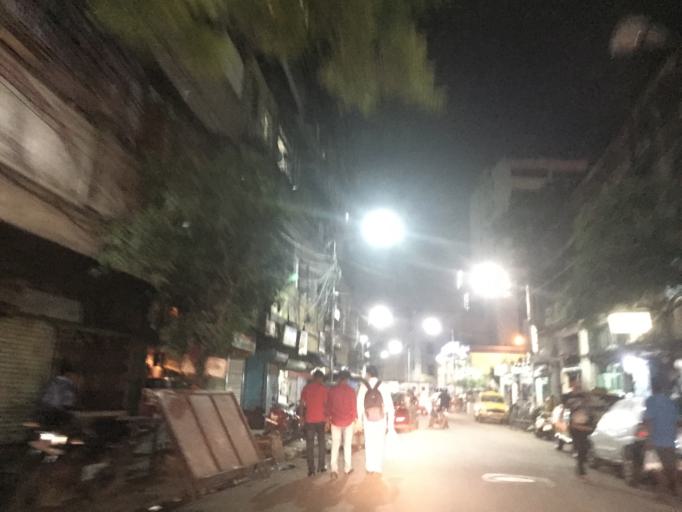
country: IN
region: West Bengal
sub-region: Kolkata
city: Bara Bazar
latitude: 22.5605
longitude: 88.3550
